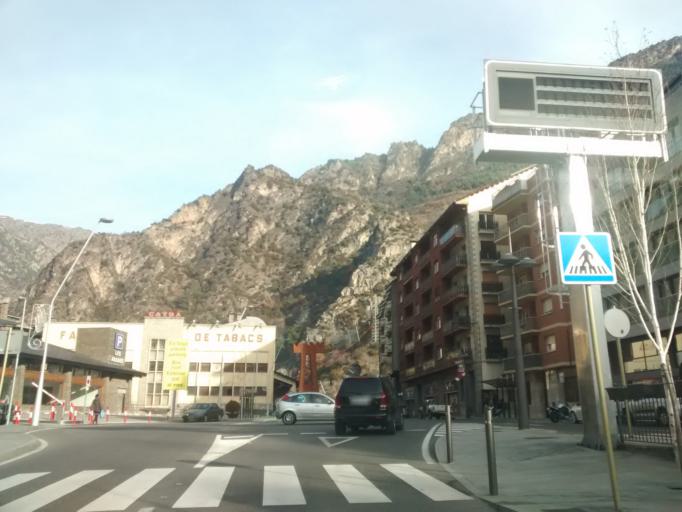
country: AD
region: Sant Julia de Loria
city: Sant Julia de Loria
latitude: 42.4710
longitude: 1.4932
